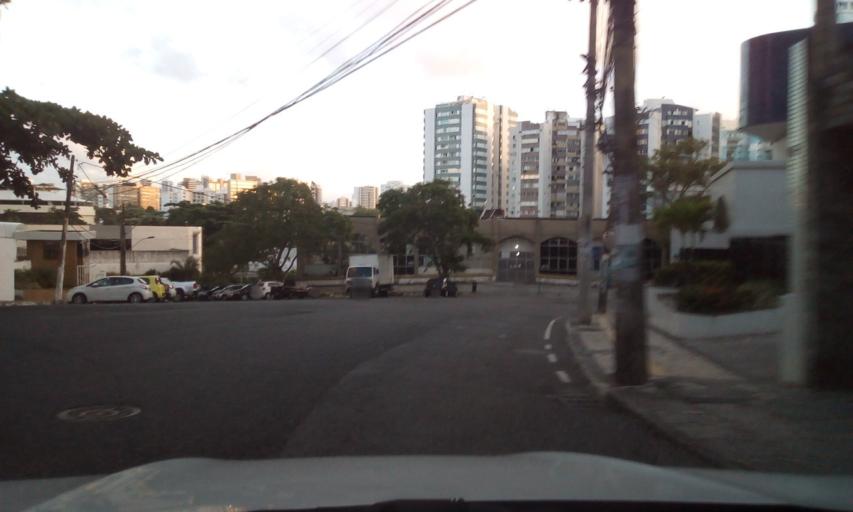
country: BR
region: Bahia
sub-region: Salvador
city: Salvador
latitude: -12.9992
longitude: -38.4633
